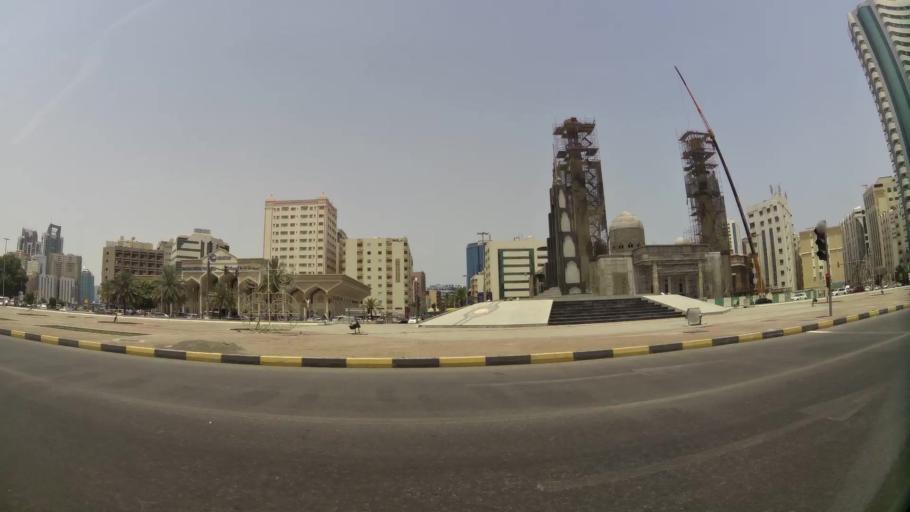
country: AE
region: Ash Shariqah
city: Sharjah
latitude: 25.3528
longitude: 55.3914
